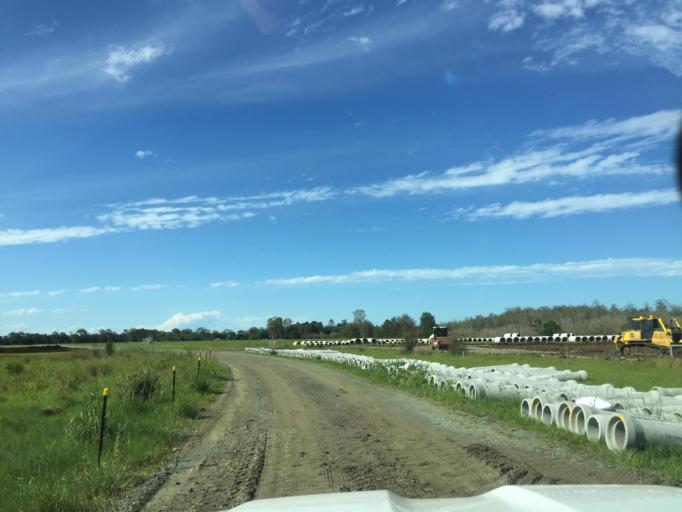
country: AU
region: Queensland
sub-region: Moreton Bay
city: Morayfield
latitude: -27.1156
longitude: 152.9942
